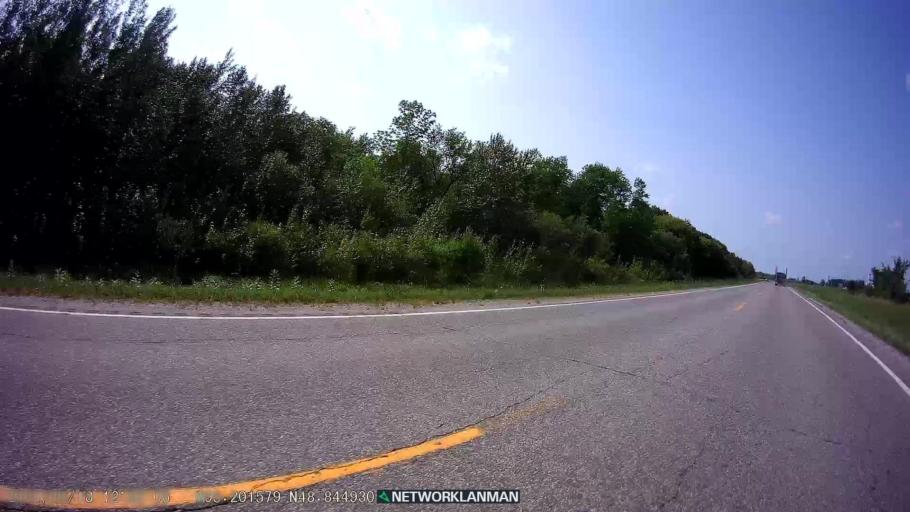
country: US
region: Minnesota
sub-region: Roseau County
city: Warroad
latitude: 48.8451
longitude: -95.2020
